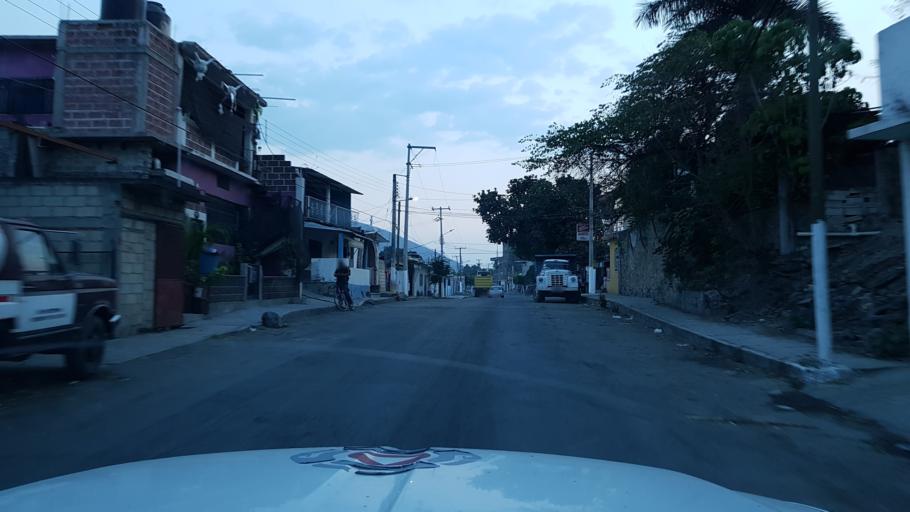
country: MX
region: Morelos
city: Tlaltizapan
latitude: 18.6930
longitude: -99.1138
